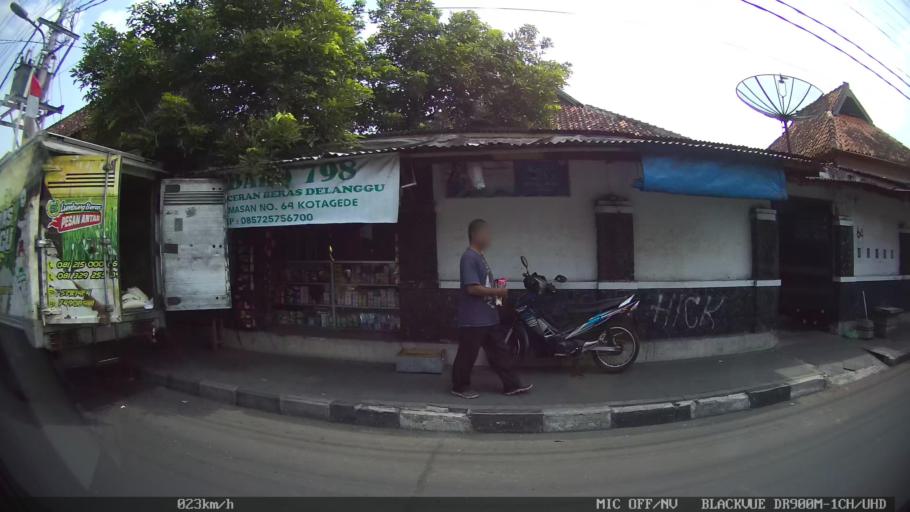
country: ID
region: Daerah Istimewa Yogyakarta
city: Yogyakarta
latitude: -7.8256
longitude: 110.4004
